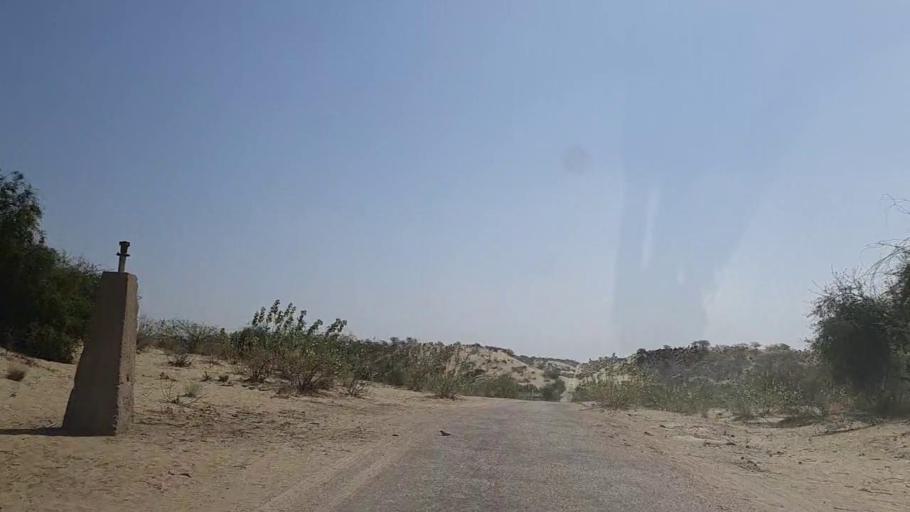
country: PK
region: Sindh
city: Diplo
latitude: 24.5125
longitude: 69.4202
